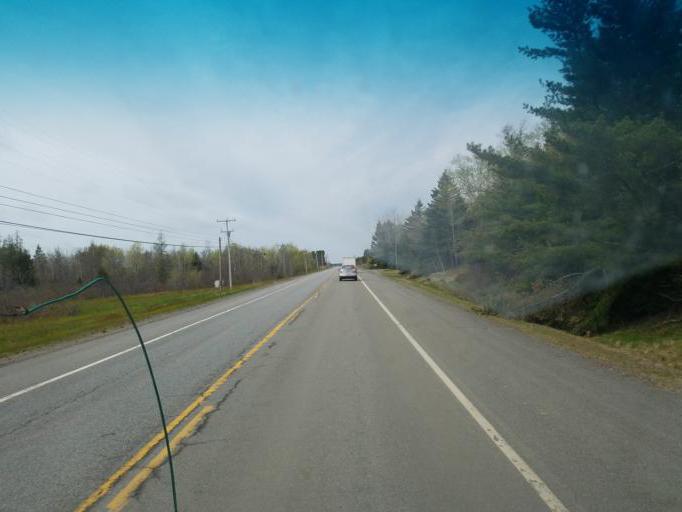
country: US
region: Maine
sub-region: Washington County
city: East Machias
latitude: 44.7633
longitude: -67.2108
